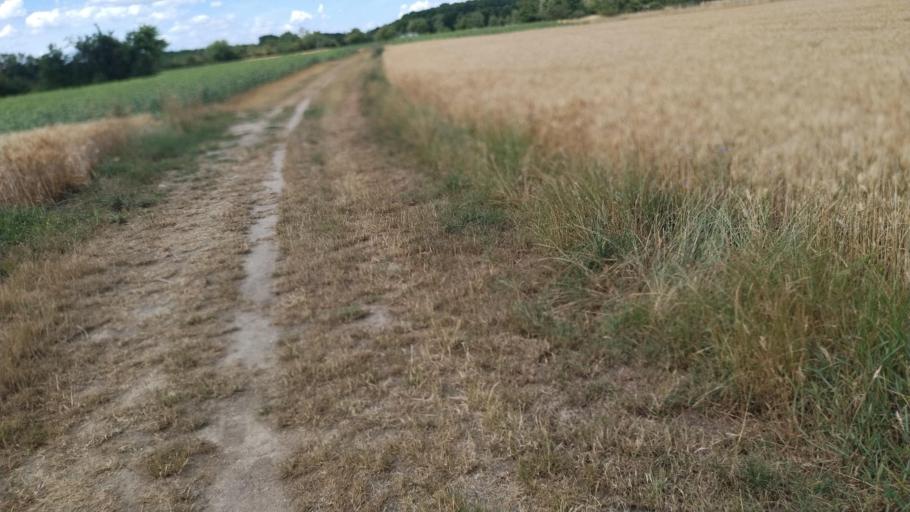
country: DE
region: Baden-Wuerttemberg
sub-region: Karlsruhe Region
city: Ubstadt-Weiher
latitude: 49.1789
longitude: 8.6106
